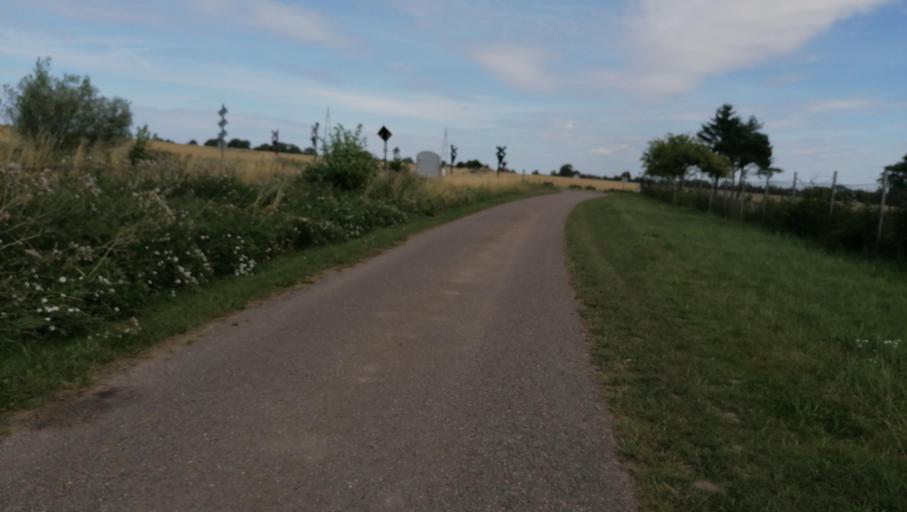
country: DK
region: Zealand
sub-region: Odsherred Kommune
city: Horve
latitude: 55.7586
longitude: 11.4604
